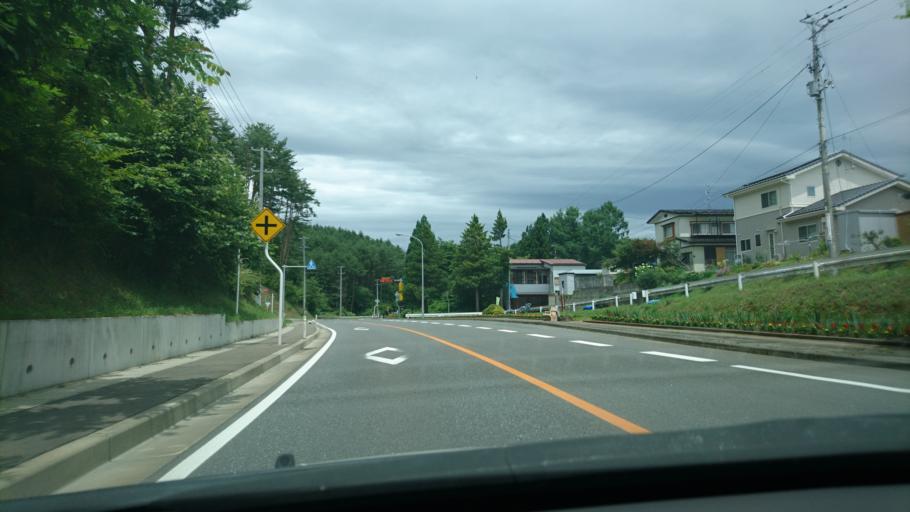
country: JP
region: Iwate
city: Miyako
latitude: 39.7117
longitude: 141.9676
